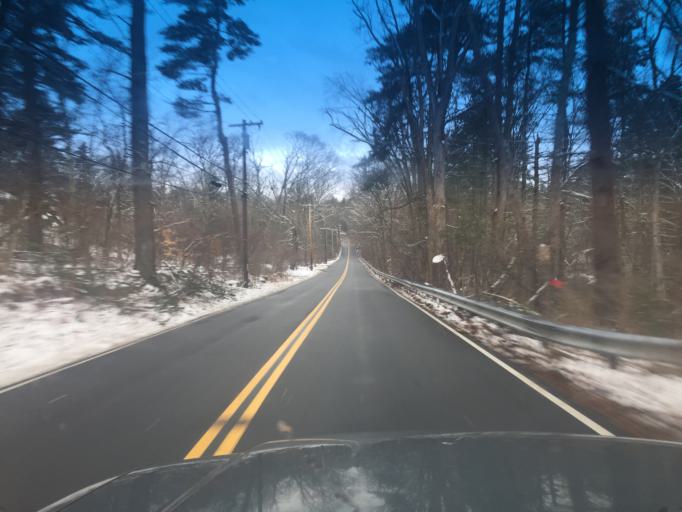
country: US
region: Massachusetts
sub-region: Norfolk County
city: Millis
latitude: 42.1888
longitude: -71.3722
